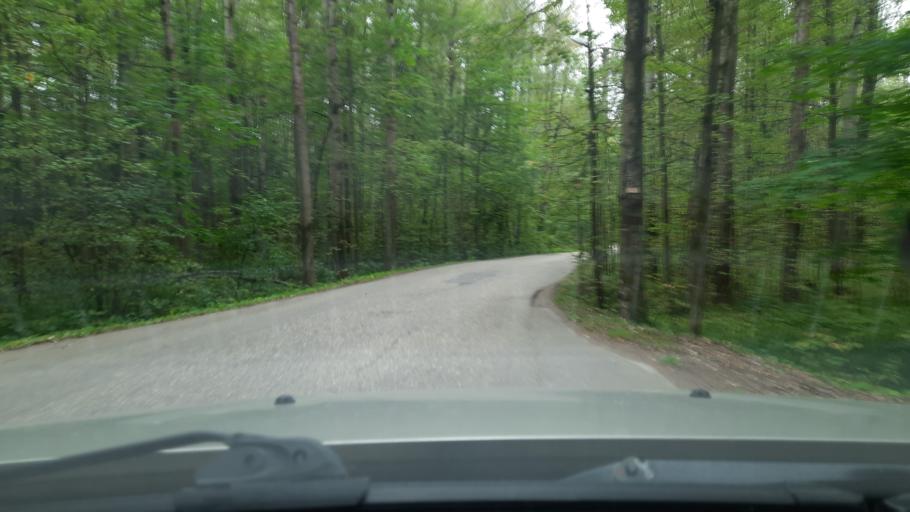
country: RU
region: Moskovskaya
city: Odintsovo
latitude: 55.7080
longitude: 37.3061
